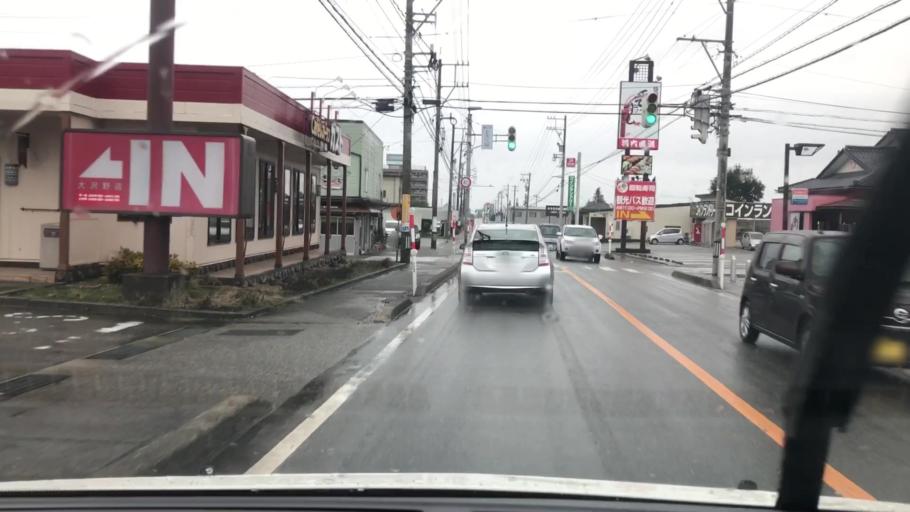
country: JP
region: Toyama
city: Yatsuomachi-higashikumisaka
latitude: 36.5869
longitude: 137.2056
